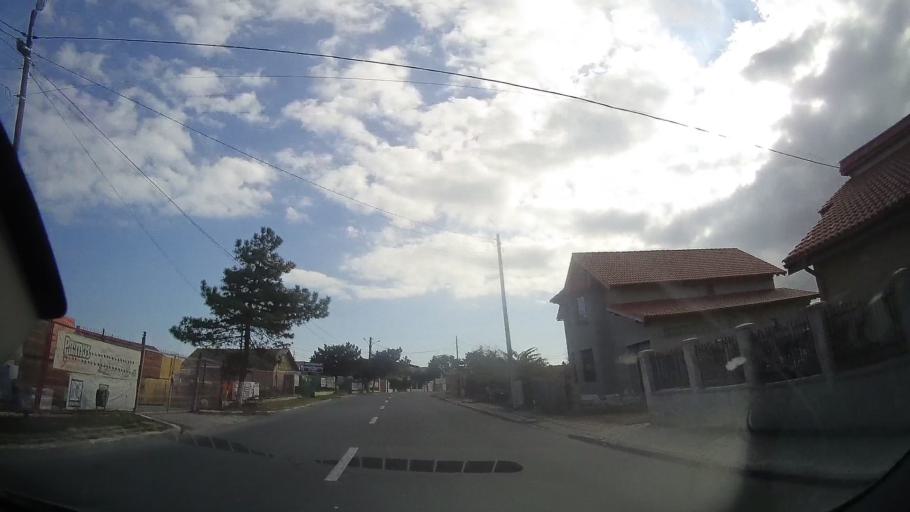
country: RO
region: Constanta
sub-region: Oras Techirghiol
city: Techirghiol
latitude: 44.0623
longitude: 28.5980
